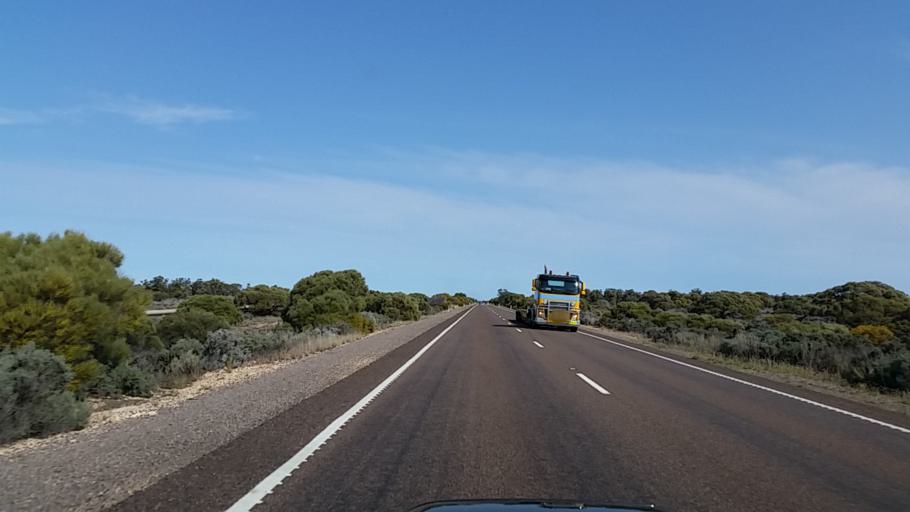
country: AU
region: South Australia
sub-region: Whyalla
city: Whyalla
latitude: -32.8080
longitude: 137.5410
